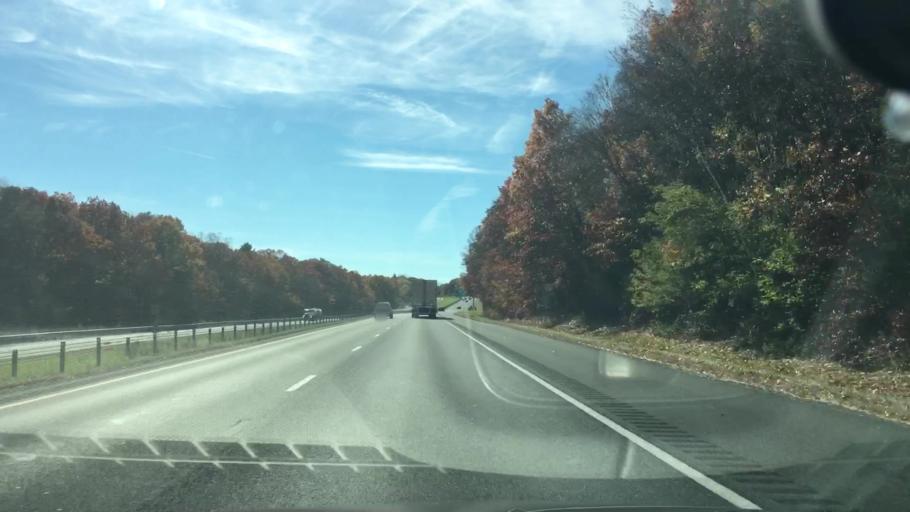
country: US
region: Massachusetts
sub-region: Hampden County
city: Holyoke
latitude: 42.2373
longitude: -72.6319
